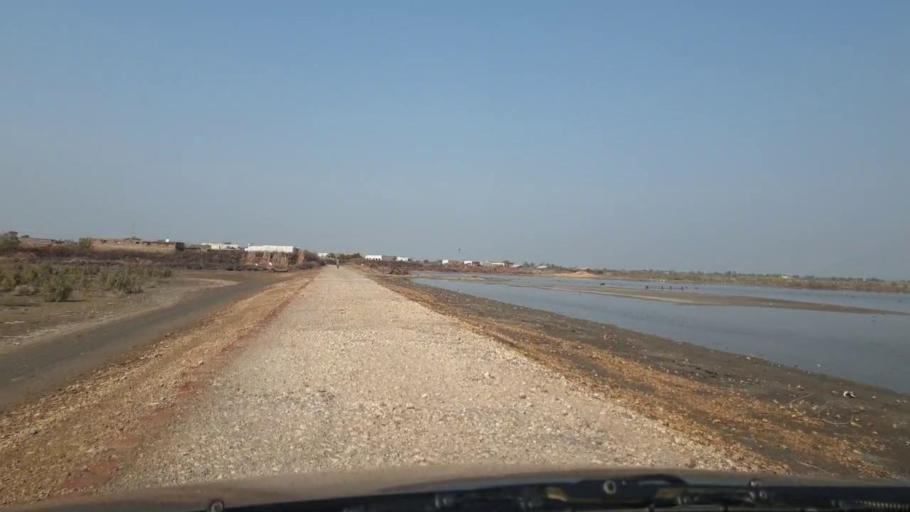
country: PK
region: Sindh
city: Jhol
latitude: 25.9033
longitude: 69.0013
